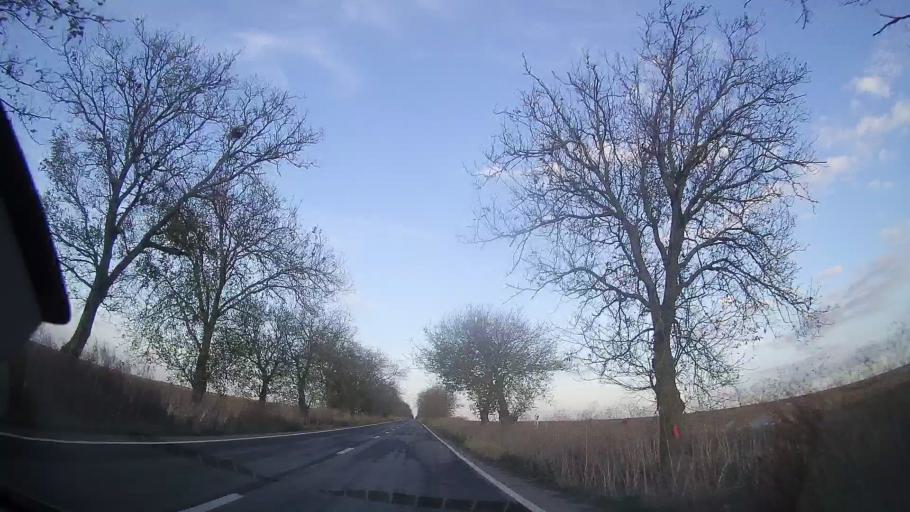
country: RO
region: Constanta
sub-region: Comuna Chirnogeni
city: Chirnogeni
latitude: 43.8593
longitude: 28.2557
